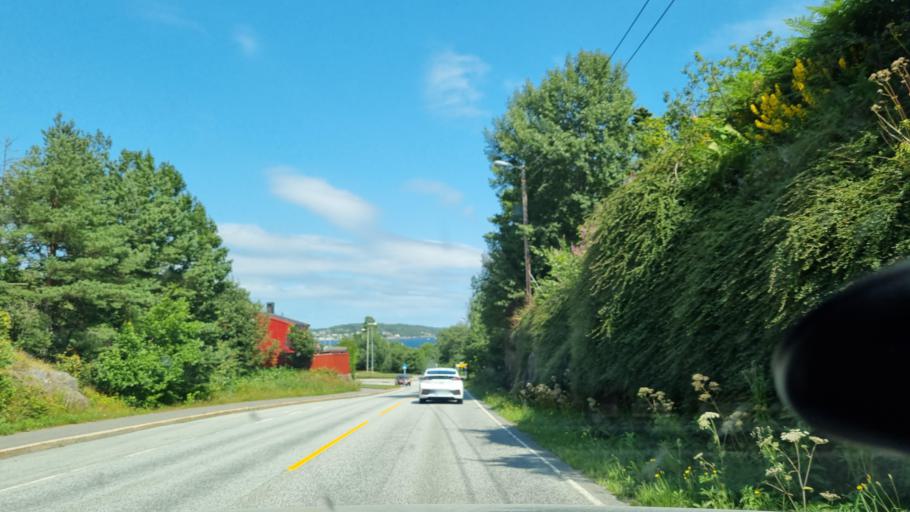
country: NO
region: Aust-Agder
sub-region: Arendal
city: Arendal
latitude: 58.4657
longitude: 8.8234
